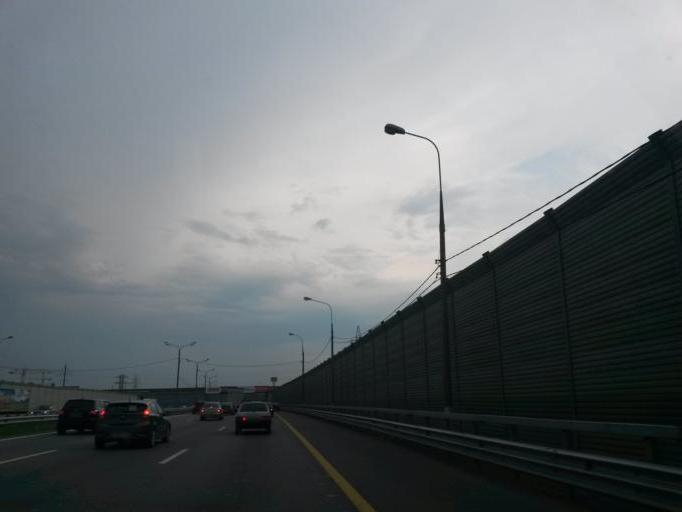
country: RU
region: Moskovskaya
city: Vostryakovo
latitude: 55.3985
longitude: 37.7786
